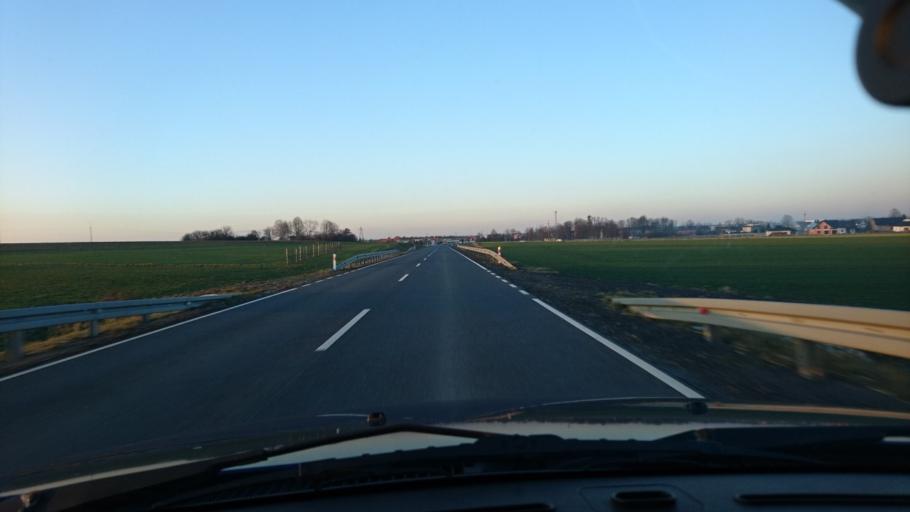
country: PL
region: Silesian Voivodeship
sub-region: Powiat gliwicki
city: Wielowies
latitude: 50.4993
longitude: 18.6060
